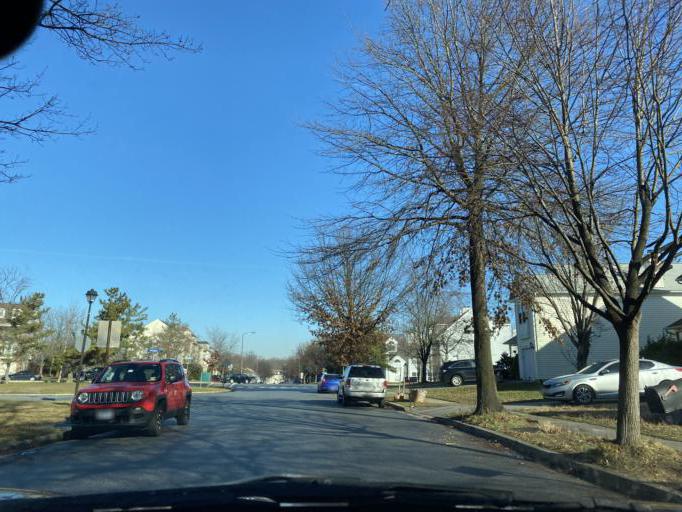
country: US
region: Maryland
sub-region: Prince George's County
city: South Laurel
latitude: 39.0838
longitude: -76.8689
